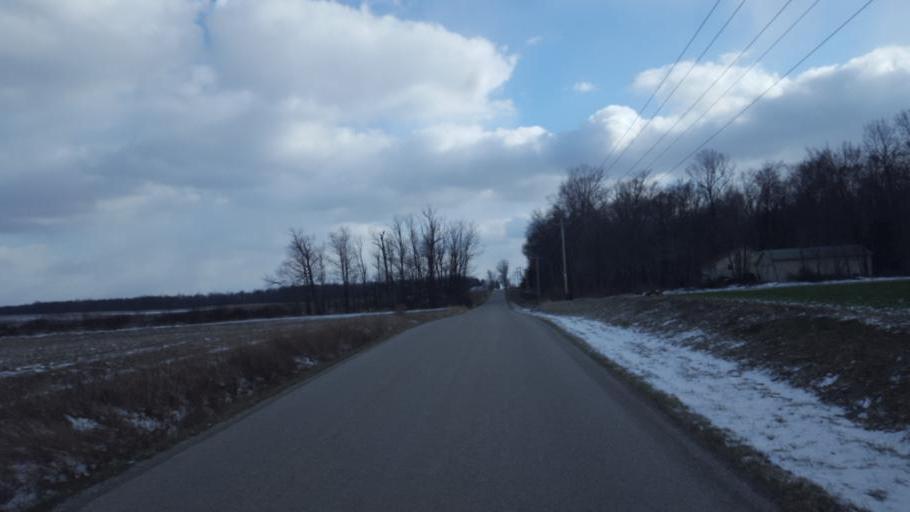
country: US
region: Ohio
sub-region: Morrow County
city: Mount Gilead
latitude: 40.6197
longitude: -82.7283
